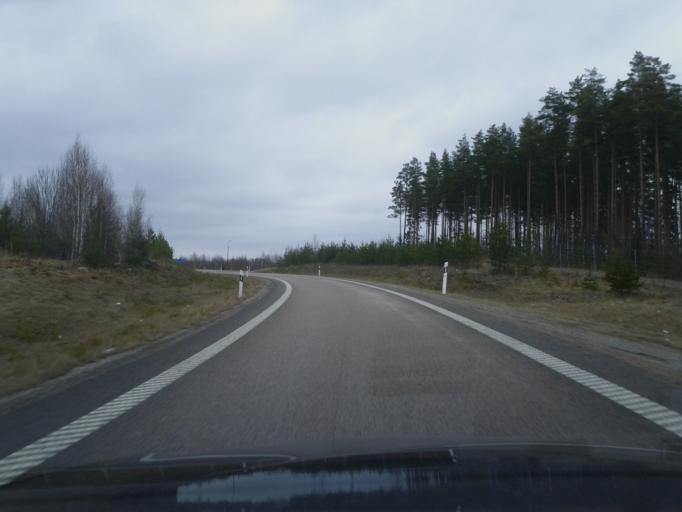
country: SE
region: Uppsala
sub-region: Osthammars Kommun
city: Bjorklinge
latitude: 60.1674
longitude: 17.5295
